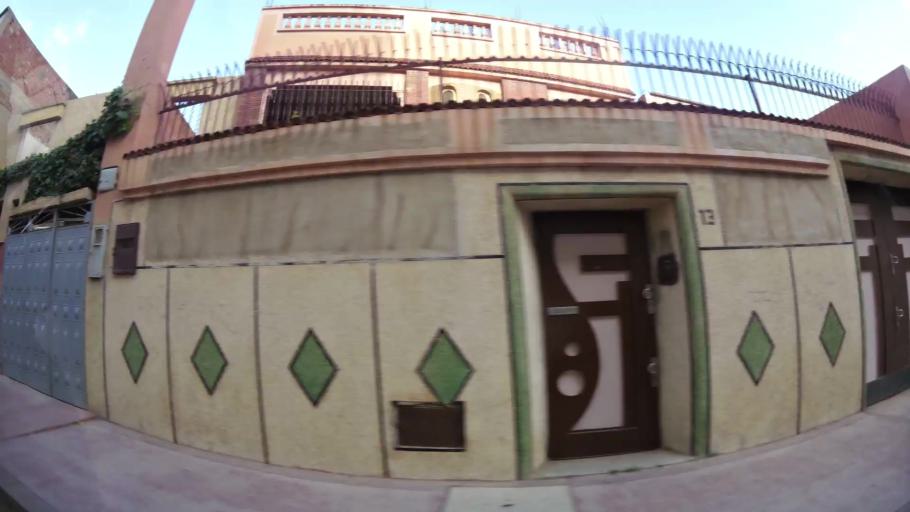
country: MA
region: Oriental
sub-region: Oujda-Angad
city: Oujda
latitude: 34.6721
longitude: -1.9235
